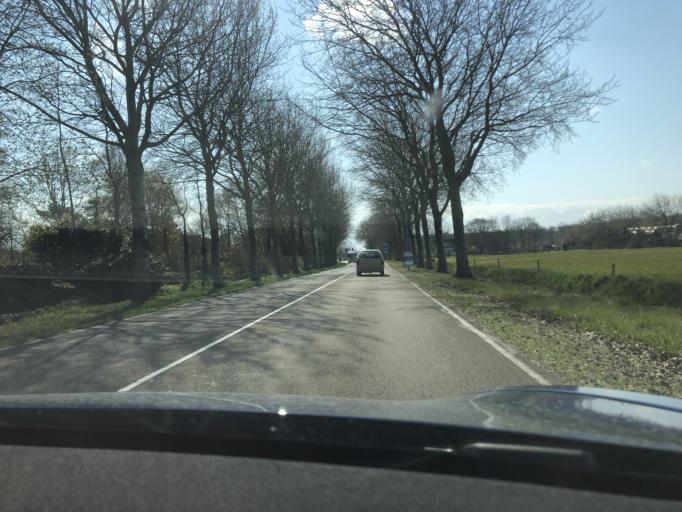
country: NL
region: Zeeland
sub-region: Gemeente Middelburg
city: Middelburg
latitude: 51.4966
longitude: 3.5903
